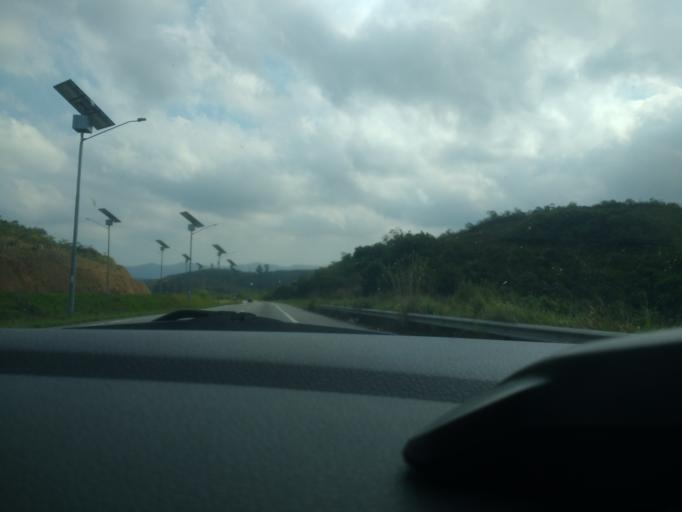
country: BR
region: Rio de Janeiro
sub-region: Queimados
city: Queimados
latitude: -22.6762
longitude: -43.5400
